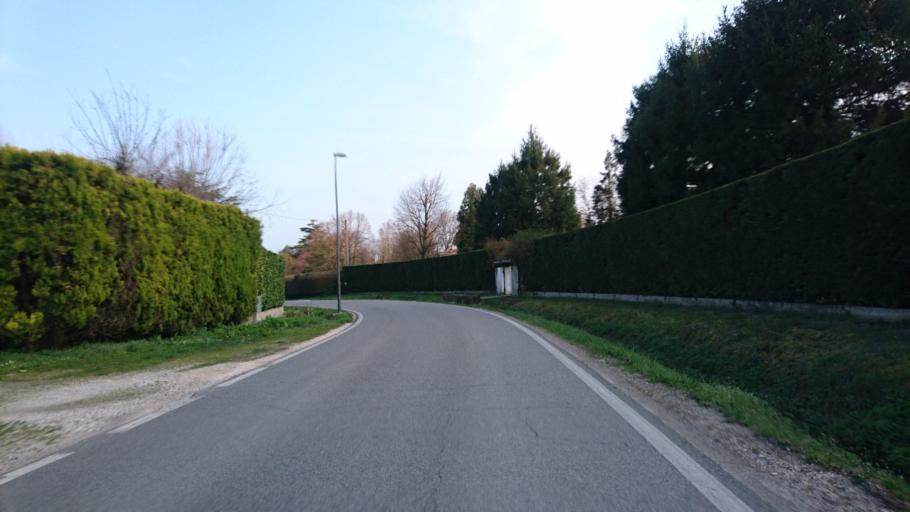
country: IT
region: Veneto
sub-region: Provincia di Padova
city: Abano Terme
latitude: 45.3687
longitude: 11.7813
